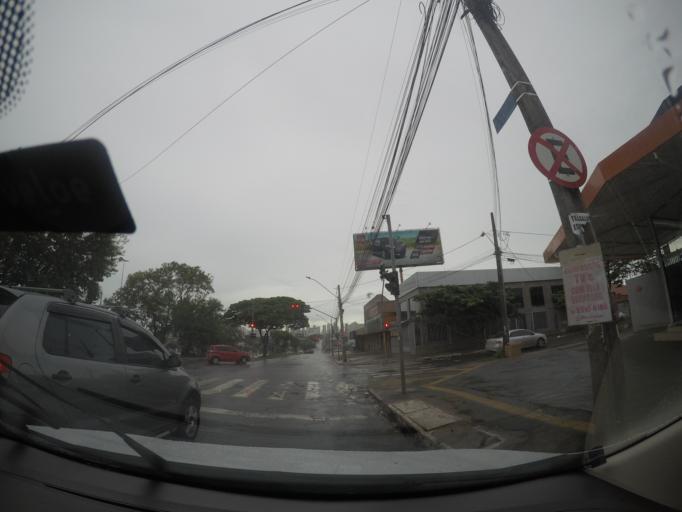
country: BR
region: Goias
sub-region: Goiania
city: Goiania
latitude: -16.7101
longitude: -49.2987
